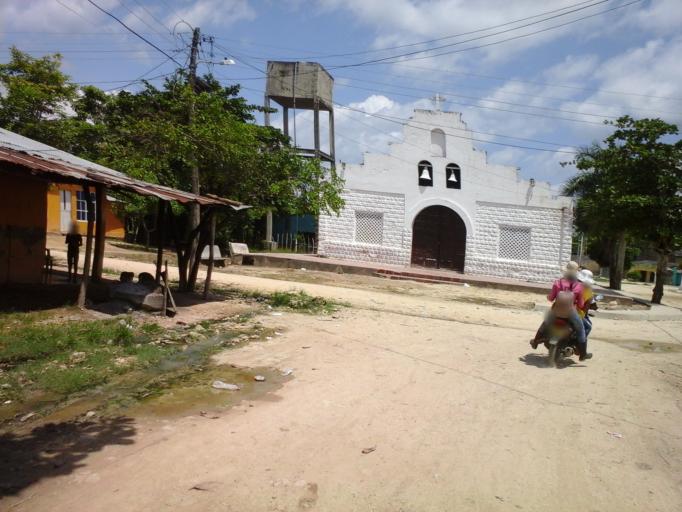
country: CO
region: Bolivar
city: San Pablo
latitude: 10.1453
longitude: -75.2773
